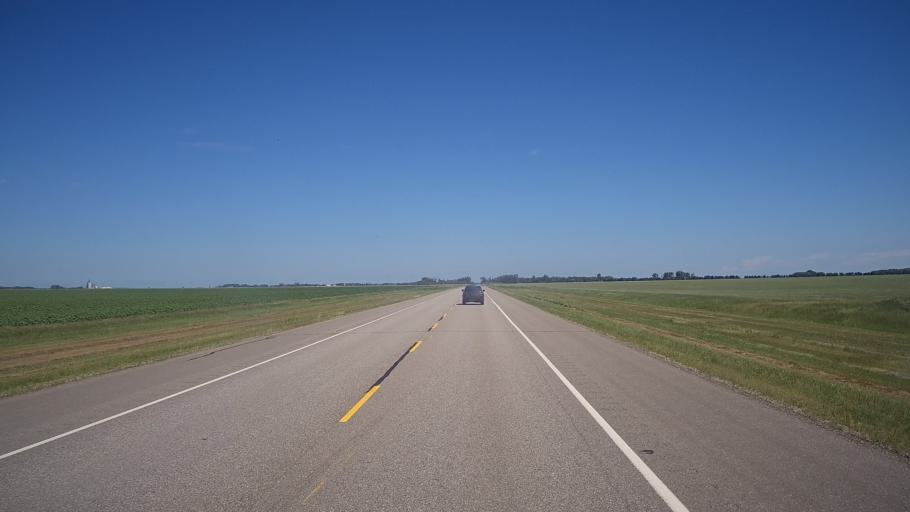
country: CA
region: Manitoba
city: Portage la Prairie
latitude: 50.0371
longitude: -98.4688
